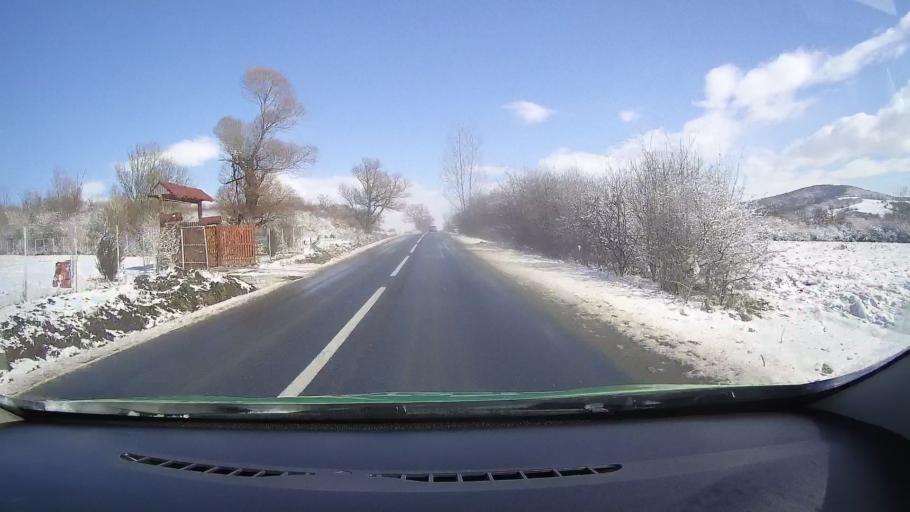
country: RO
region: Sibiu
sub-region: Comuna Nocrich
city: Nocrich
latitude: 45.8435
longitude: 24.4246
